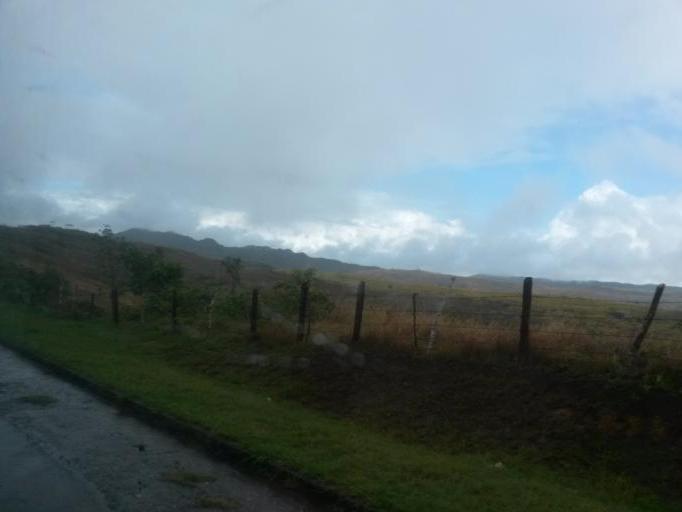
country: CO
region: Cauca
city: El Bordo
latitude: 2.1506
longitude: -76.9176
